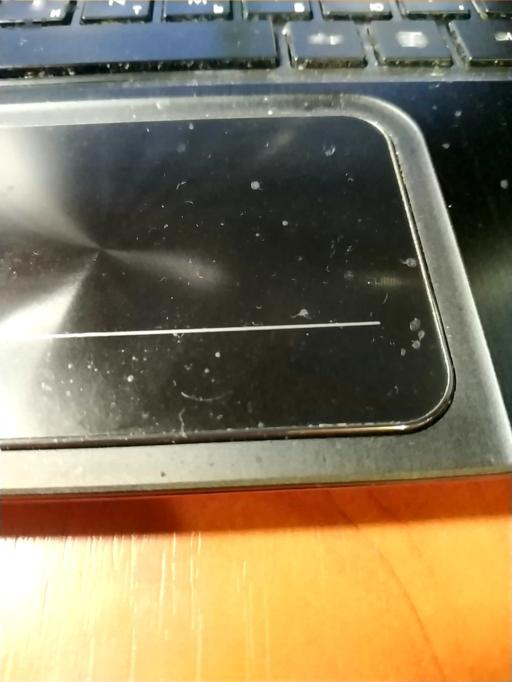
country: RU
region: Rjazan
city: Skopin
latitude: 53.9258
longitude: 39.5316
